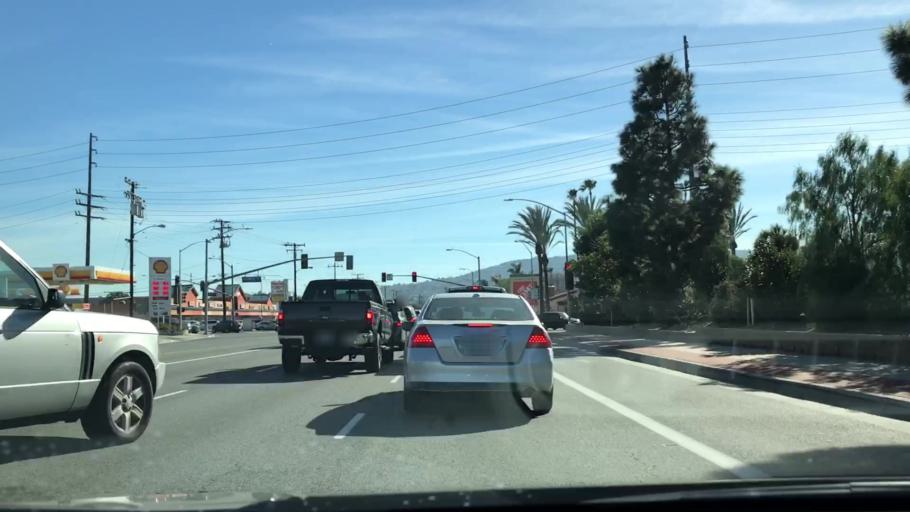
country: US
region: California
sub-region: Los Angeles County
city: Lomita
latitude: 33.8067
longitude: -118.3281
